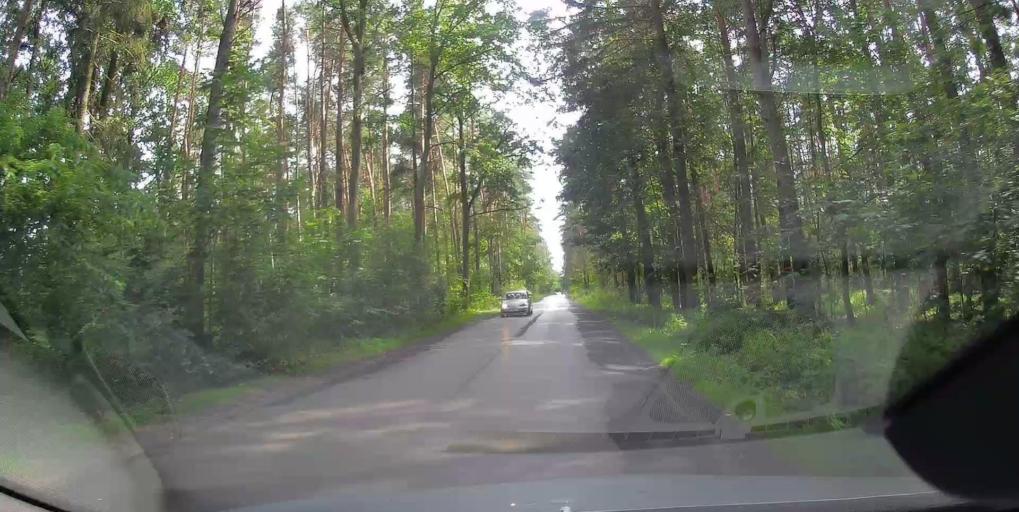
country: PL
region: Lodz Voivodeship
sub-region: Powiat tomaszowski
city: Tomaszow Mazowiecki
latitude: 51.4809
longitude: 19.9876
